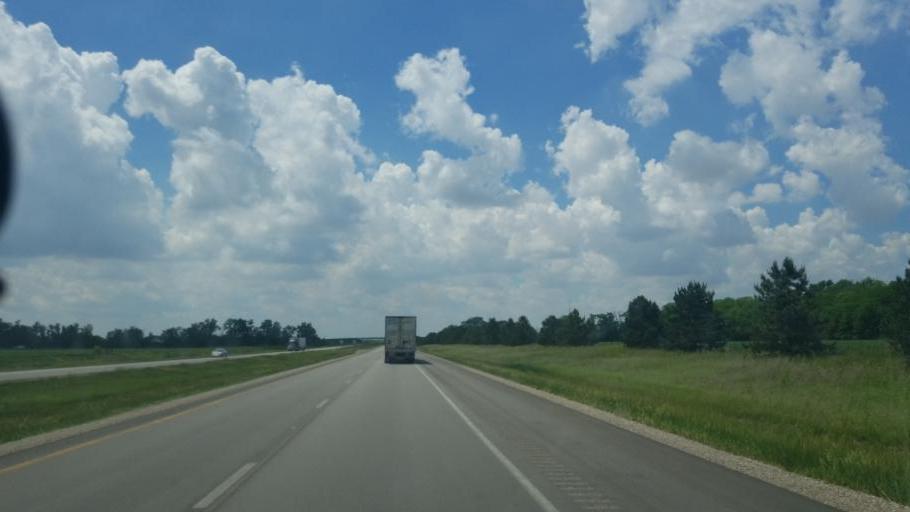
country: US
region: Ohio
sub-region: Van Wert County
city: Van Wert
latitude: 40.8699
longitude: -84.4643
